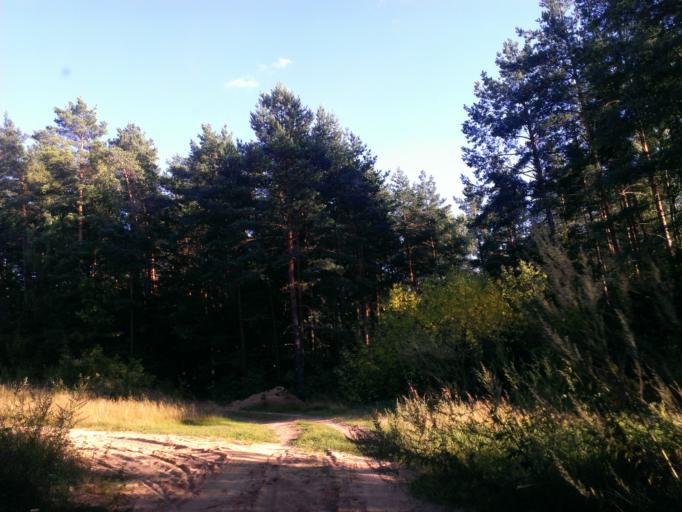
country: LV
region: Riga
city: Bergi
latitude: 57.0134
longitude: 24.2390
